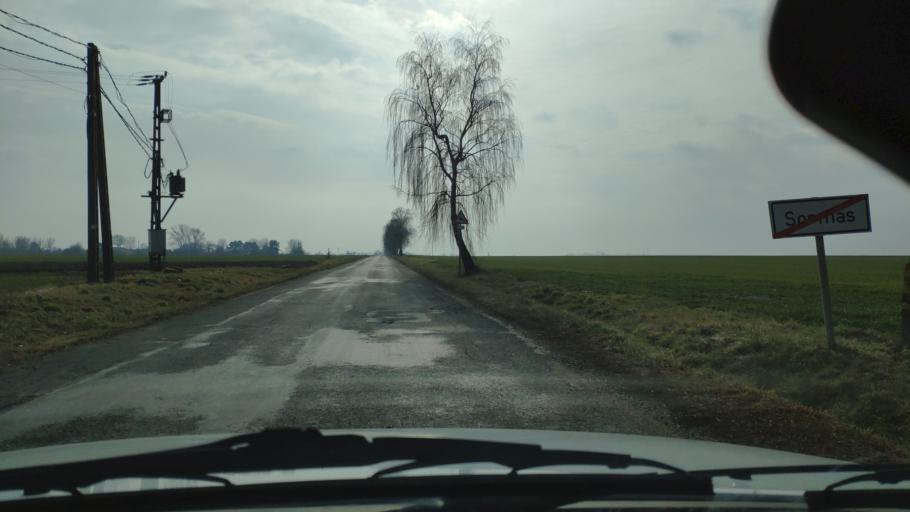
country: HU
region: Zala
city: Nagykanizsa
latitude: 46.4509
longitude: 16.9124
